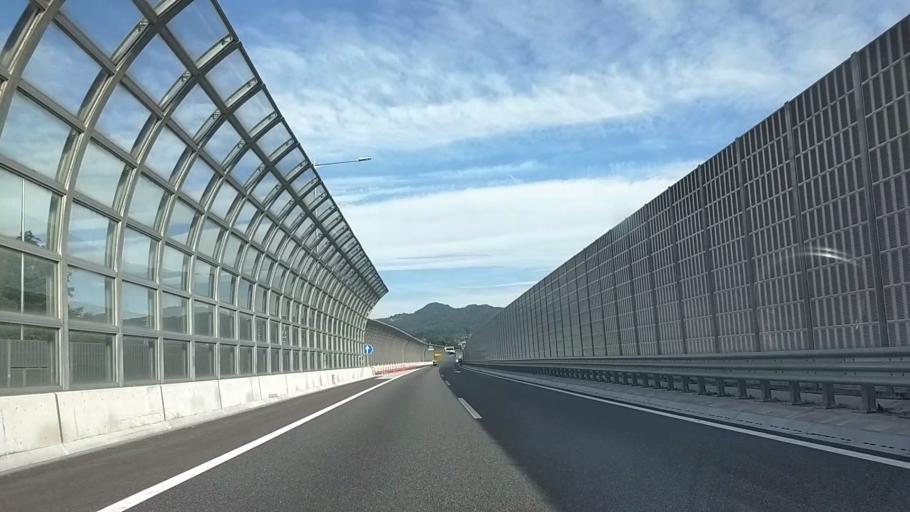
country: JP
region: Tokyo
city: Hachioji
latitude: 35.5823
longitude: 139.2926
